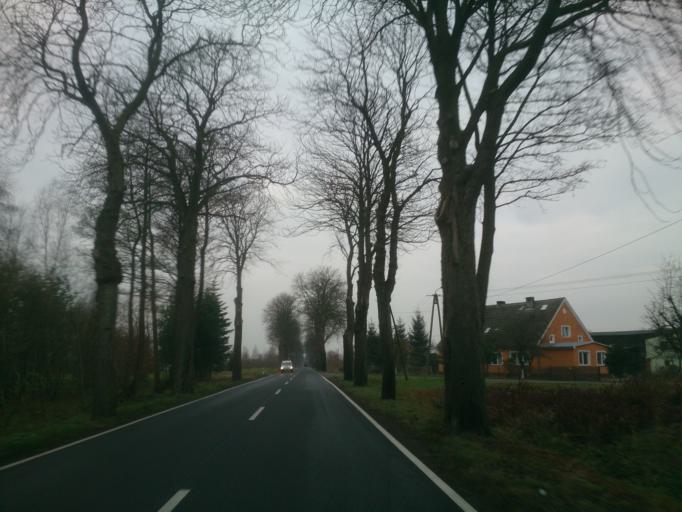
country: PL
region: West Pomeranian Voivodeship
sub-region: Powiat slawienski
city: Darlowo
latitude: 54.3901
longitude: 16.4585
